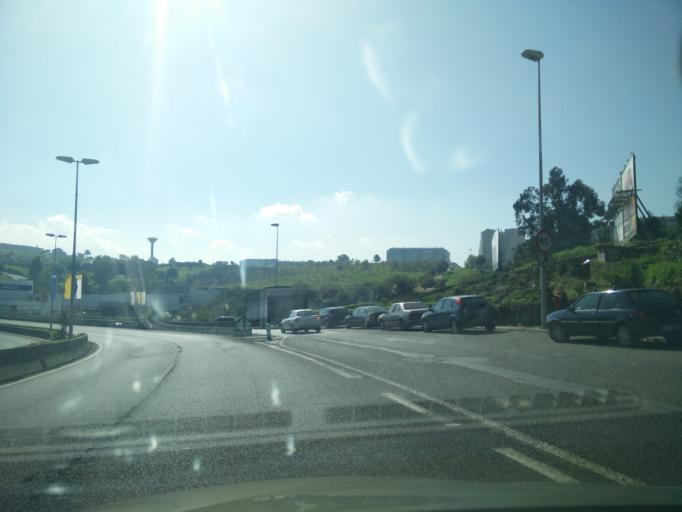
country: ES
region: Galicia
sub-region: Provincia da Coruna
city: A Coruna
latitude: 43.3501
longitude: -8.3909
